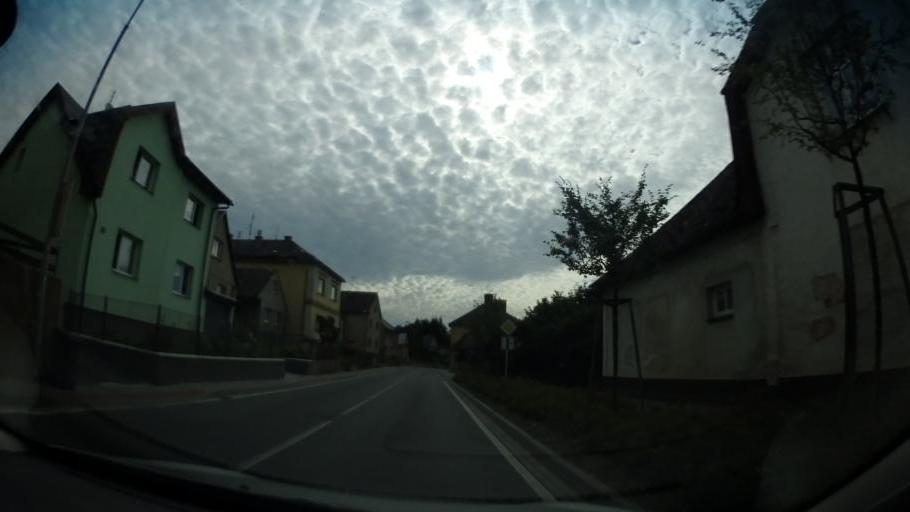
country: CZ
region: Olomoucky
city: Zabreh
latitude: 49.8861
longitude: 16.8690
